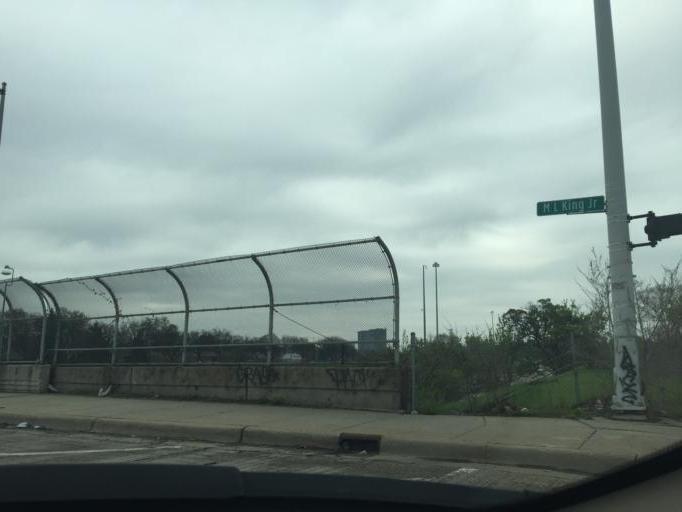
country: US
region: Michigan
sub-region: Wayne County
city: Detroit
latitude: 42.3360
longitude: -83.0910
